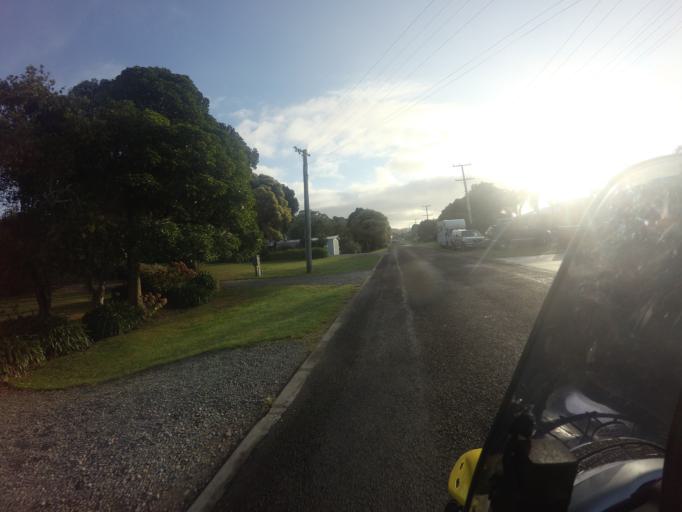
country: NZ
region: Gisborne
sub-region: Gisborne District
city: Gisborne
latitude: -38.6757
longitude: 178.0814
